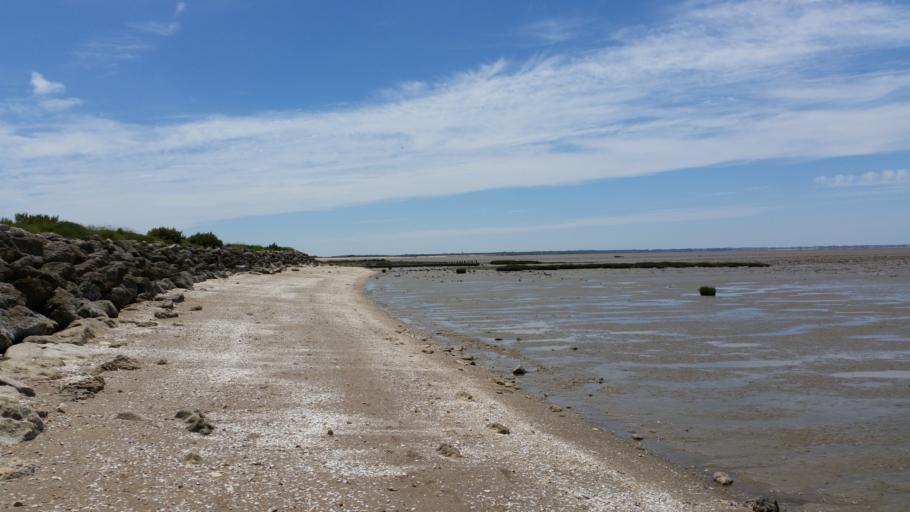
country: FR
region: Poitou-Charentes
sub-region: Departement de la Charente-Maritime
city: Port-des-Barques
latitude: 45.9208
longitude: -1.0739
